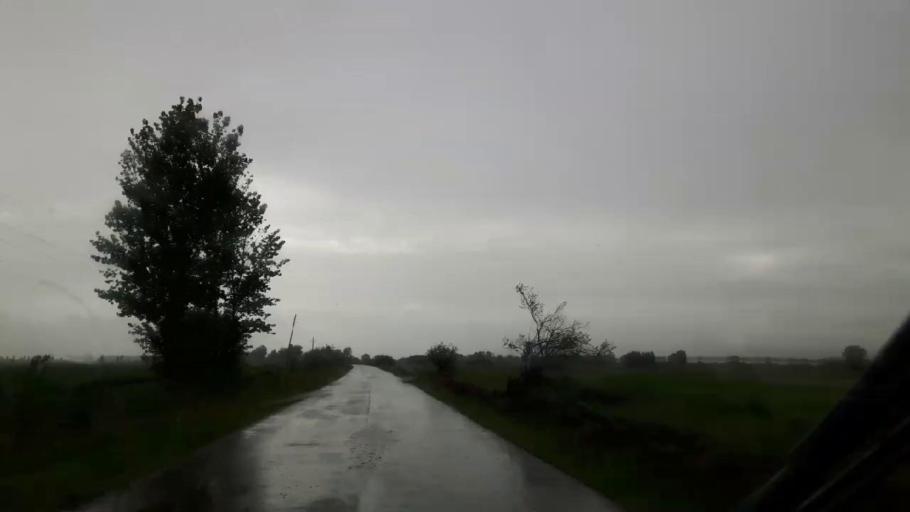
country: GE
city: Agara
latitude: 42.0146
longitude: 43.8103
